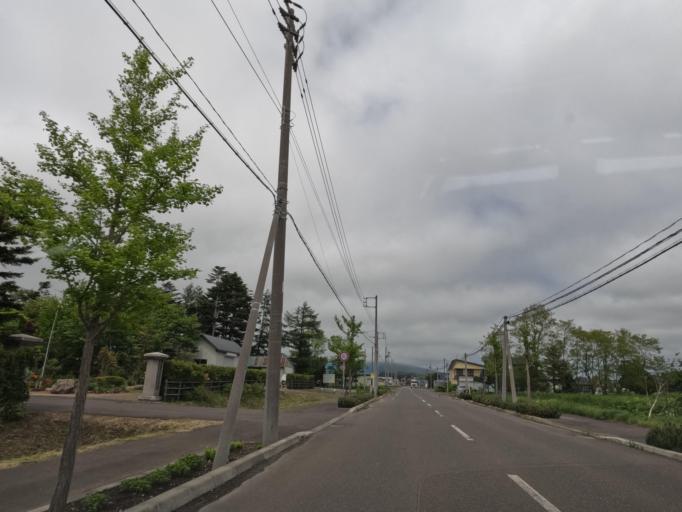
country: JP
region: Hokkaido
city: Tobetsu
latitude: 43.2397
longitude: 141.5133
